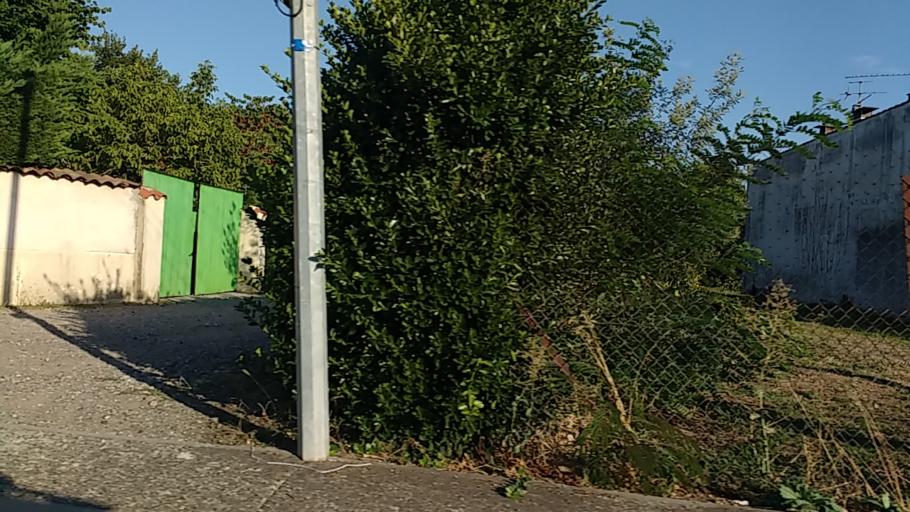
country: FR
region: Midi-Pyrenees
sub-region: Departement de la Haute-Garonne
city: Cugnaux
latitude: 43.5580
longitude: 1.3657
